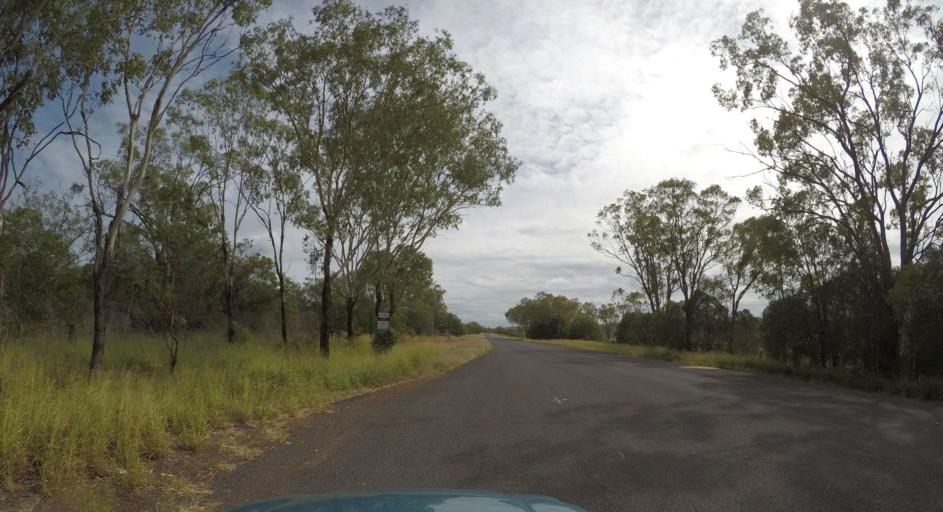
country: AU
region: Queensland
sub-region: Western Downs
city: Dalby
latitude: -27.0479
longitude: 151.3121
